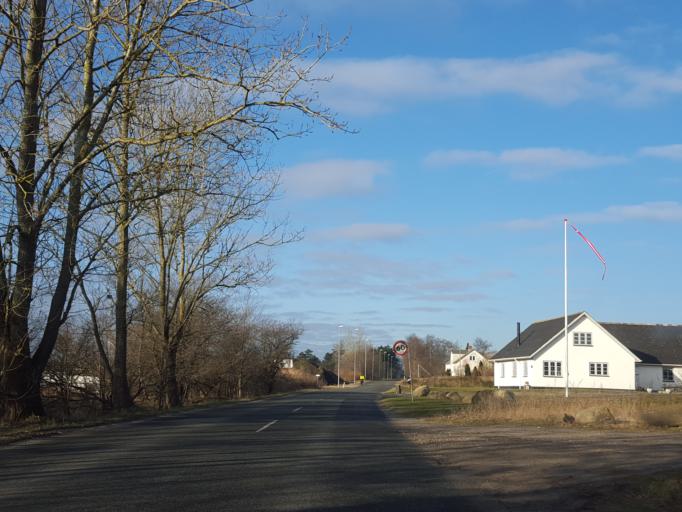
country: DK
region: North Denmark
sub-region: Alborg Kommune
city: Gistrup
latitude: 57.0029
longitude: 9.9565
